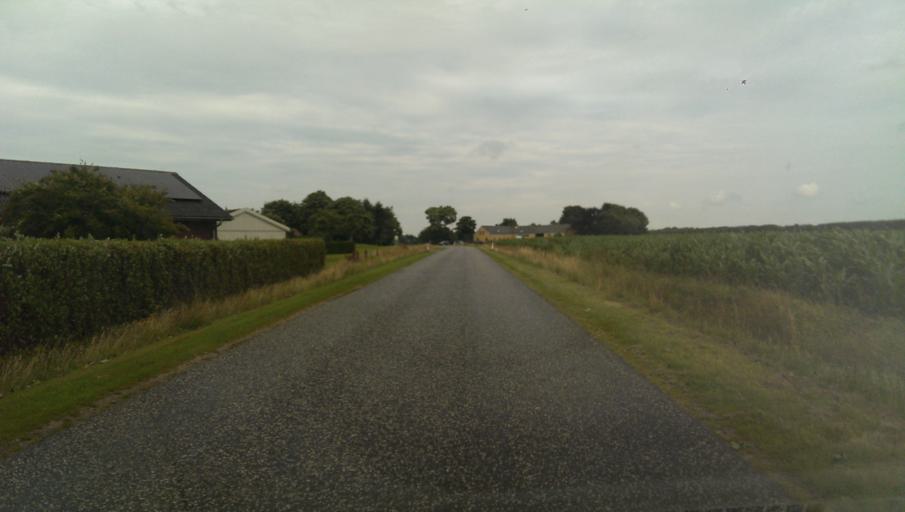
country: DK
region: South Denmark
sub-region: Esbjerg Kommune
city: Bramming
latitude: 55.4682
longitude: 8.7263
